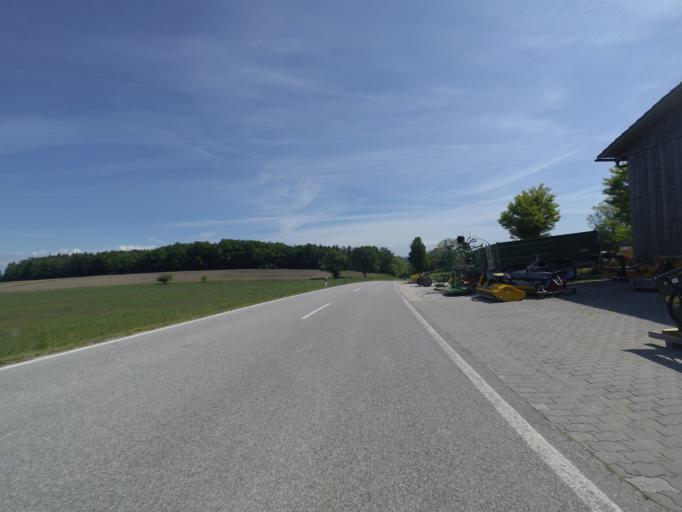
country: DE
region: Bavaria
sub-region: Upper Bavaria
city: Petting
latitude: 47.9065
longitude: 12.7997
